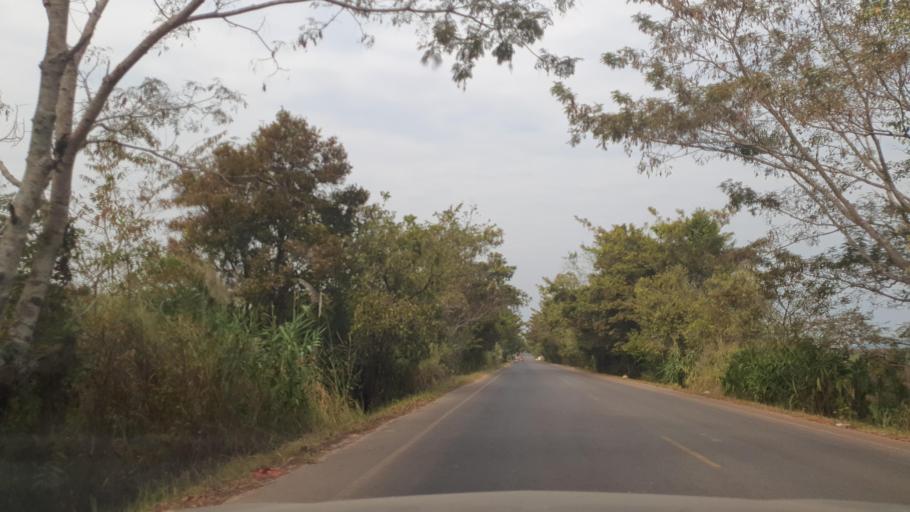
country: TH
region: Changwat Bueng Kan
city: Bung Khla
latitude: 18.2211
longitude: 104.0374
